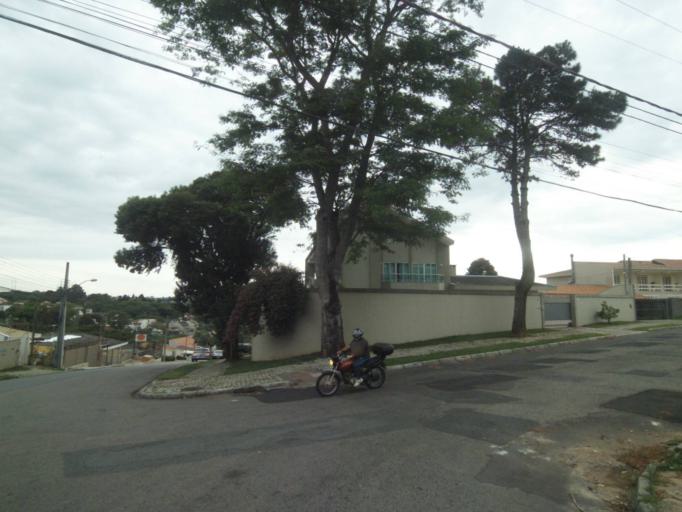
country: BR
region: Parana
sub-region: Curitiba
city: Curitiba
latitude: -25.3950
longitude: -49.2917
